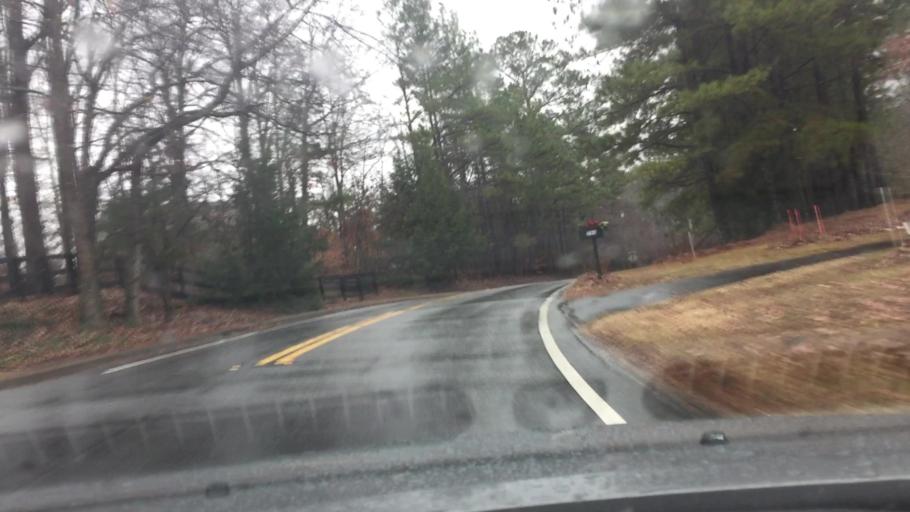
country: US
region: Georgia
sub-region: Cobb County
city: Kennesaw
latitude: 33.9720
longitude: -84.6348
